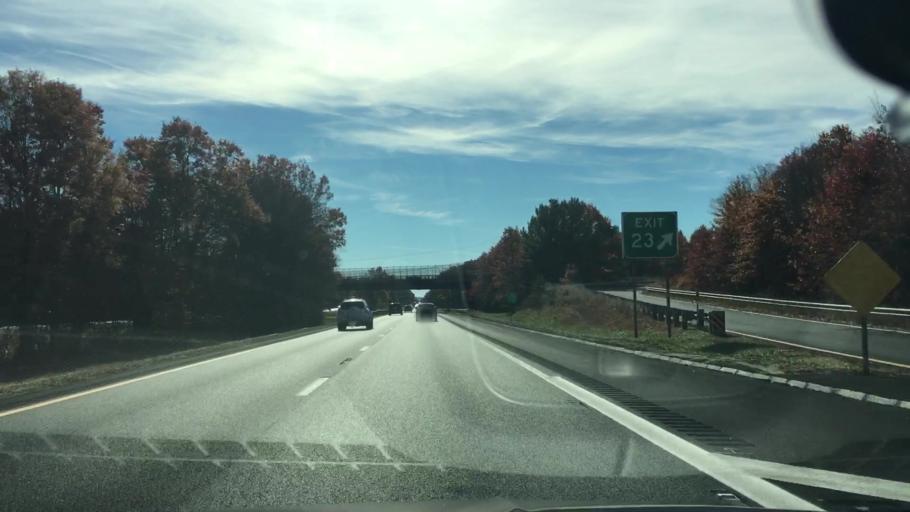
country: US
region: Massachusetts
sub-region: Franklin County
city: Whately
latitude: 42.4343
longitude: -72.6220
